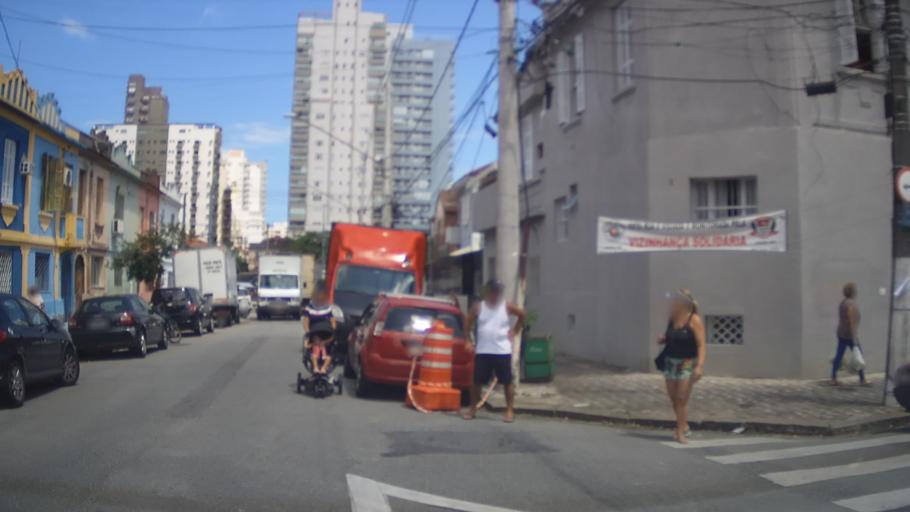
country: BR
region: Sao Paulo
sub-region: Santos
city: Santos
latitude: -23.9620
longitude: -46.3419
